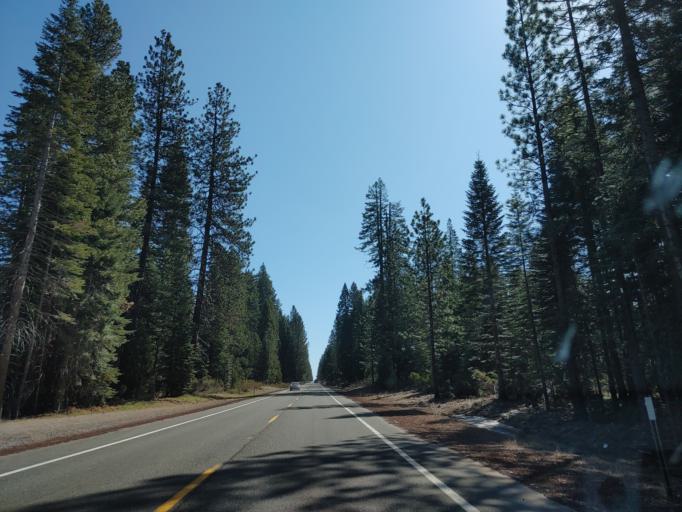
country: US
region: California
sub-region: Siskiyou County
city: McCloud
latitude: 41.2545
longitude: -122.0689
